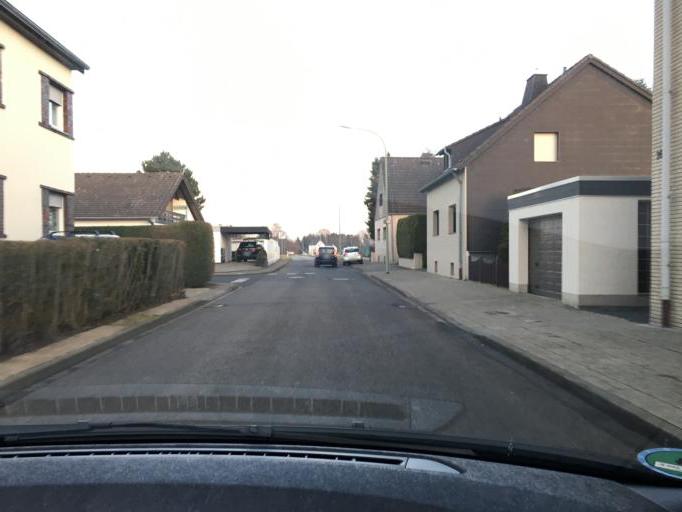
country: DE
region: North Rhine-Westphalia
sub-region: Regierungsbezirk Koln
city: Kreuzau
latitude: 50.7747
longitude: 6.4525
